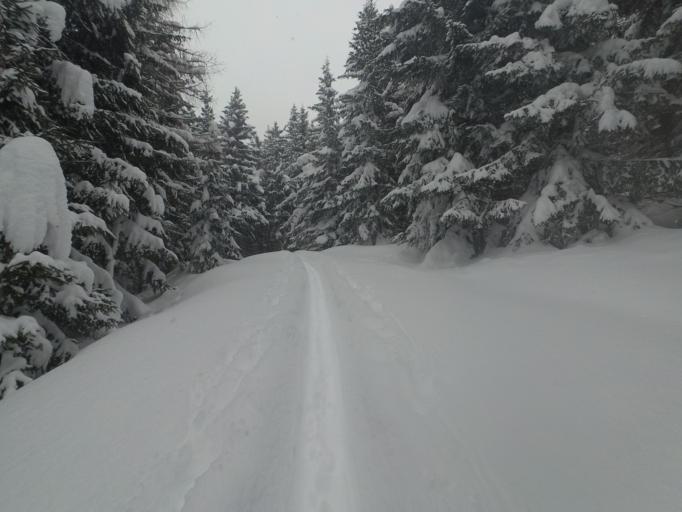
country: AT
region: Salzburg
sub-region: Politischer Bezirk Sankt Johann im Pongau
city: Sankt Johann im Pongau
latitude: 47.3127
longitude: 13.2131
